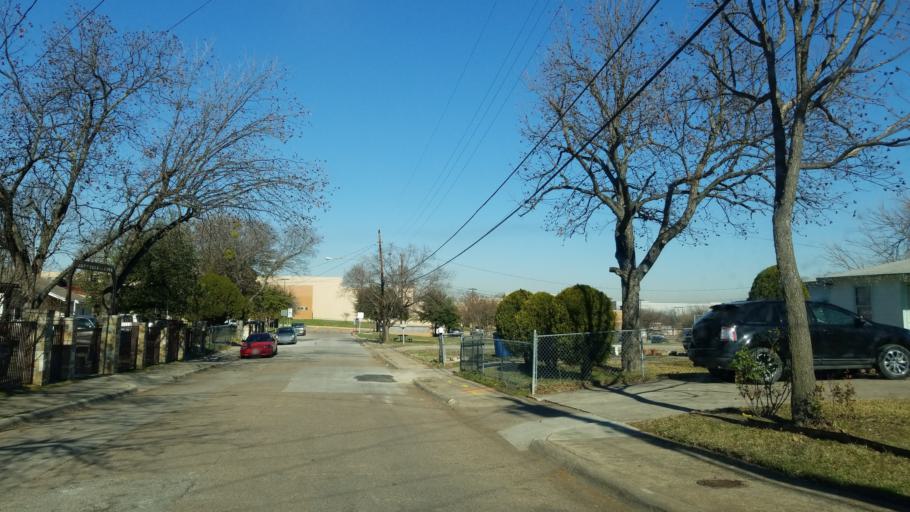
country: US
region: Texas
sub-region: Dallas County
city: Cockrell Hill
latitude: 32.7573
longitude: -96.9101
